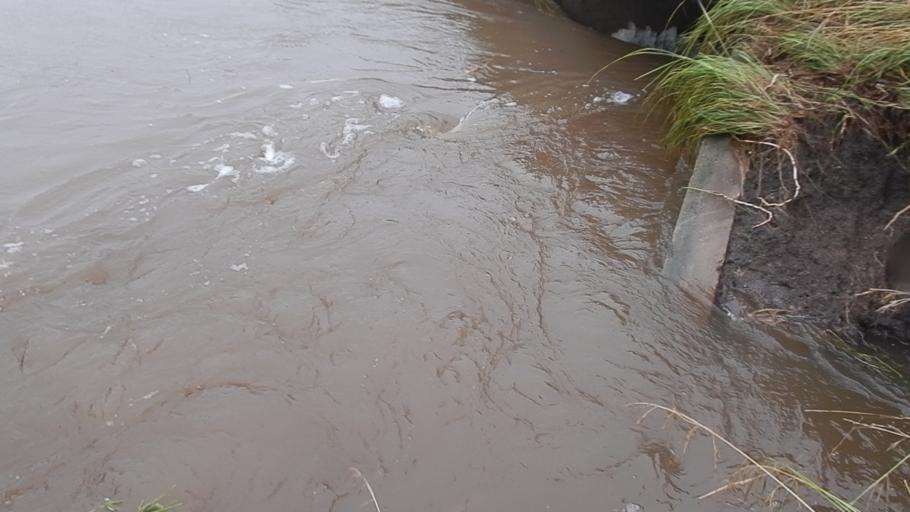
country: AR
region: Santa Fe
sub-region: Departamento de San Justo
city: San Justo
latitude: -30.7584
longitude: -60.5616
